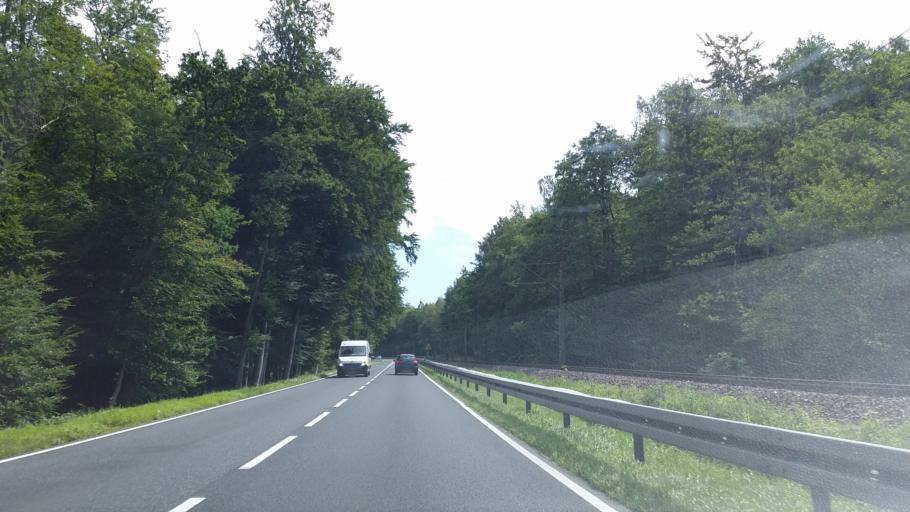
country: PL
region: West Pomeranian Voivodeship
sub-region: Powiat kolobrzeski
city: Dygowo
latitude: 54.1867
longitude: 15.6726
